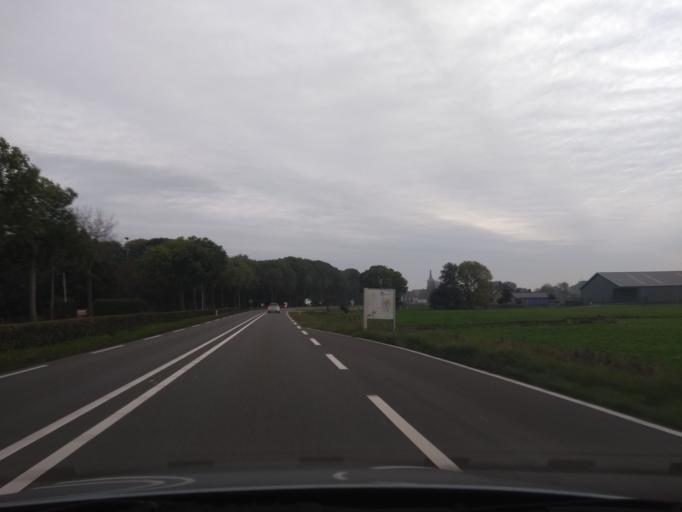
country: NL
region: Overijssel
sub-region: Gemeente Zwartewaterland
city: Hasselt
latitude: 52.5979
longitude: 6.0962
